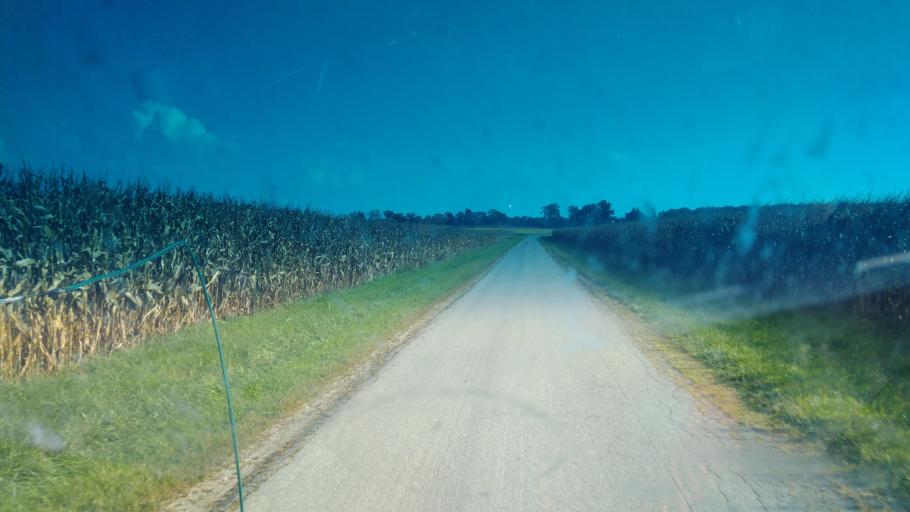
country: US
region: Ohio
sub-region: Wyandot County
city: Upper Sandusky
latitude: 40.8937
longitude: -83.2429
